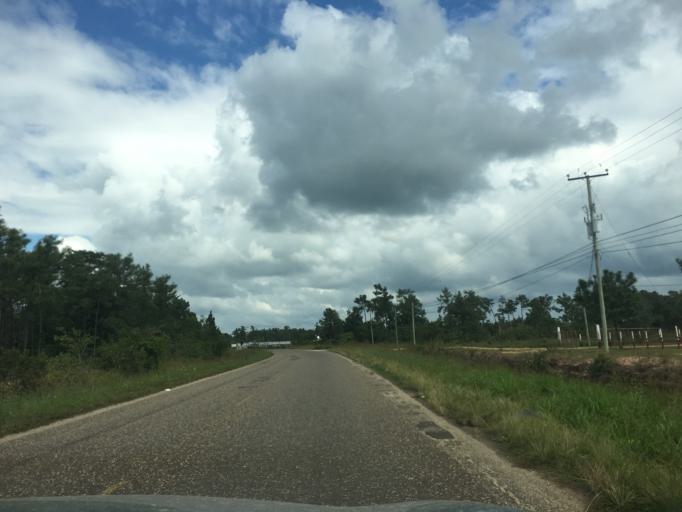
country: BZ
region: Stann Creek
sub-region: Dangriga
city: Dangriga
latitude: 16.8906
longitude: -88.3384
